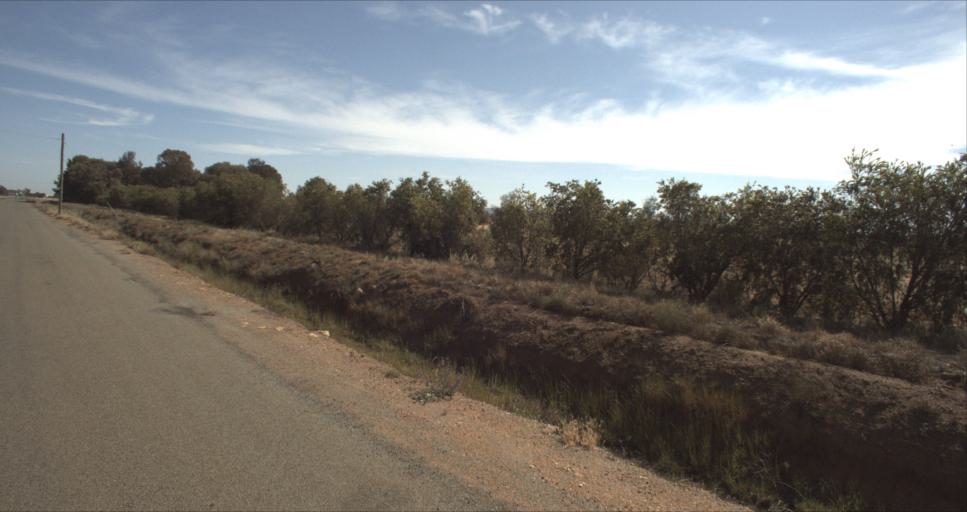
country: AU
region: New South Wales
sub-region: Leeton
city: Leeton
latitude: -34.5734
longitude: 146.4756
